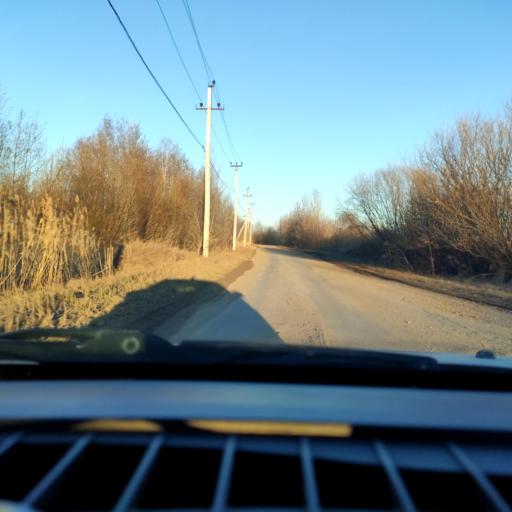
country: RU
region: Perm
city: Kultayevo
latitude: 57.9524
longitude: 55.9897
